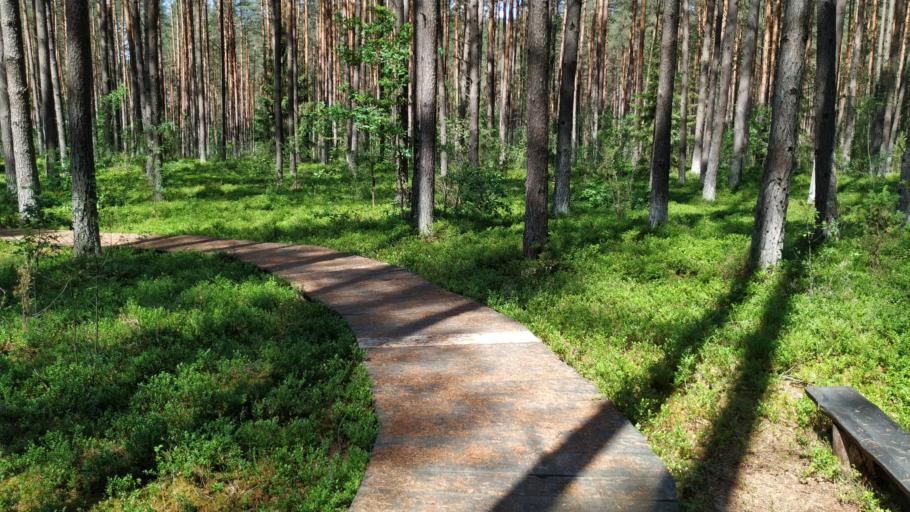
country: LT
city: Nemencine
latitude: 54.8092
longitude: 25.3973
